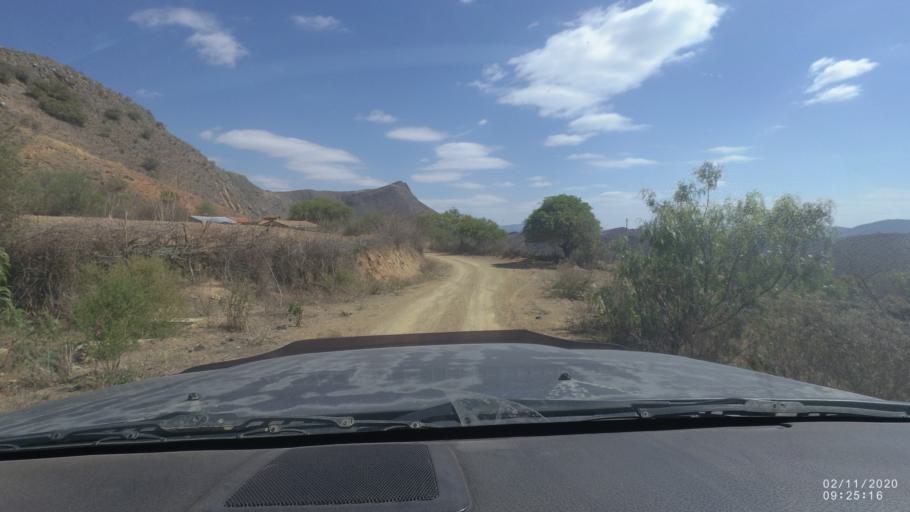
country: BO
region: Chuquisaca
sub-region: Provincia Zudanez
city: Mojocoya
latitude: -18.4556
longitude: -64.5825
